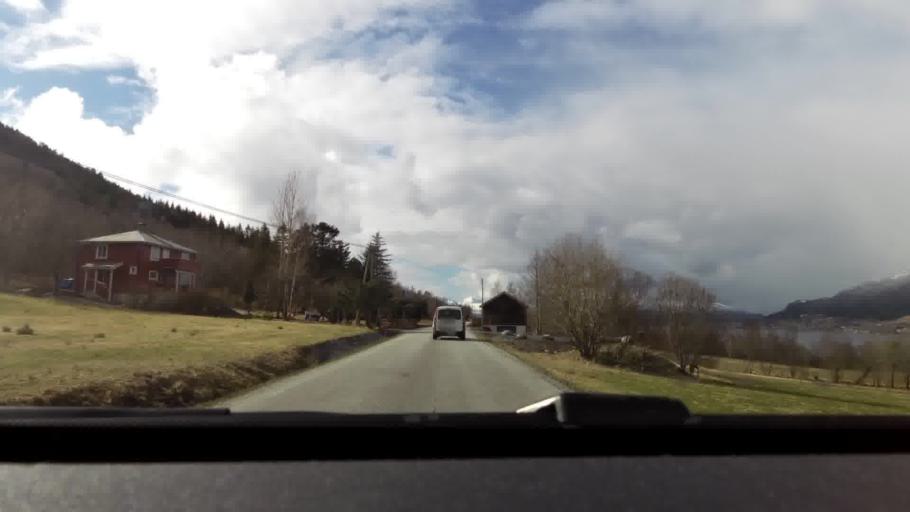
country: NO
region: More og Romsdal
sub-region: Gjemnes
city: Batnfjordsora
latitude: 62.9660
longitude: 7.6879
